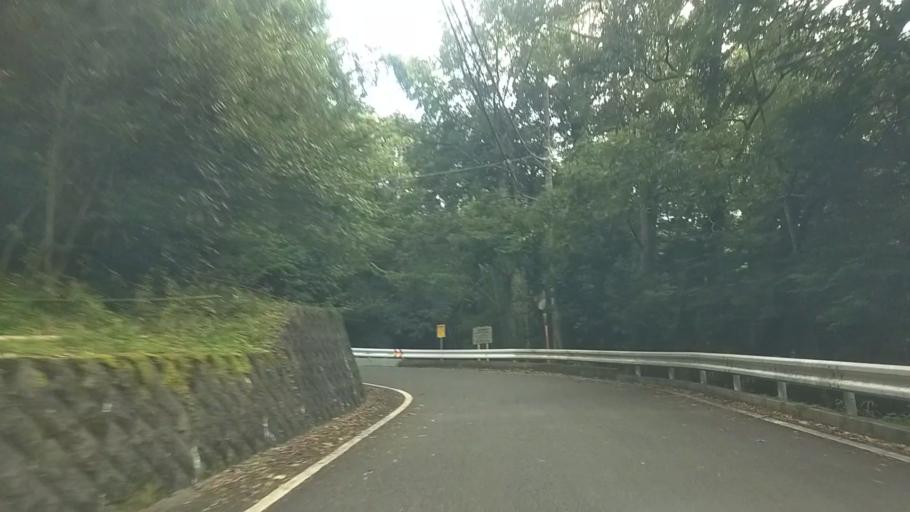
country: JP
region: Shizuoka
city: Ito
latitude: 34.9865
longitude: 138.9775
